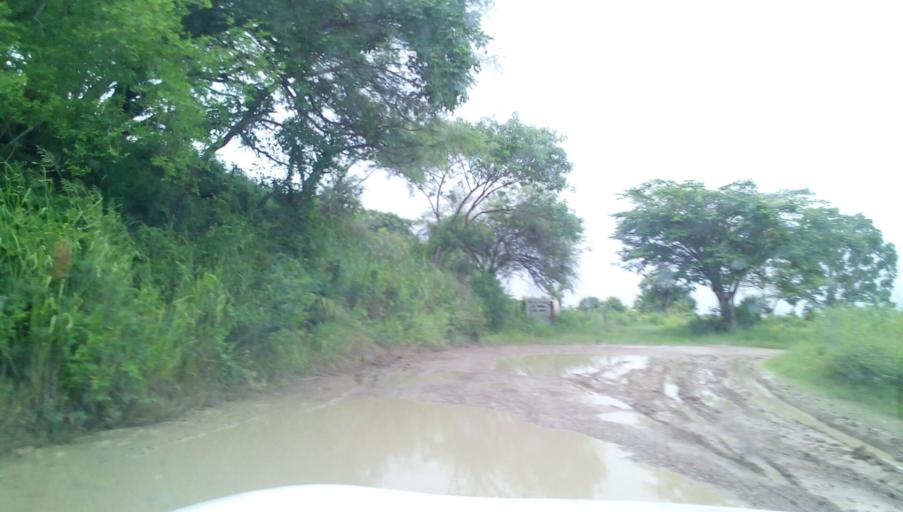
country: MX
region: Veracruz
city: Panuco
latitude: 21.8079
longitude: -98.1061
